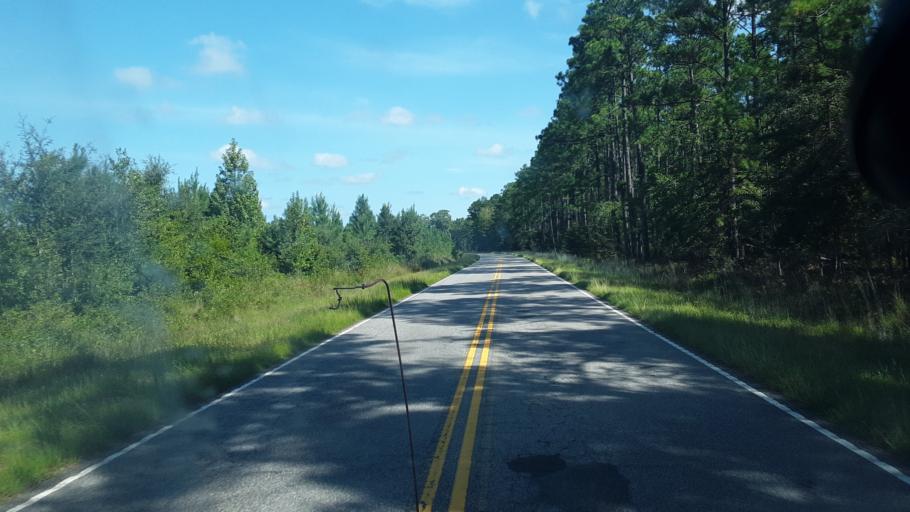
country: US
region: South Carolina
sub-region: Hampton County
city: Varnville
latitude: 32.7142
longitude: -81.0288
